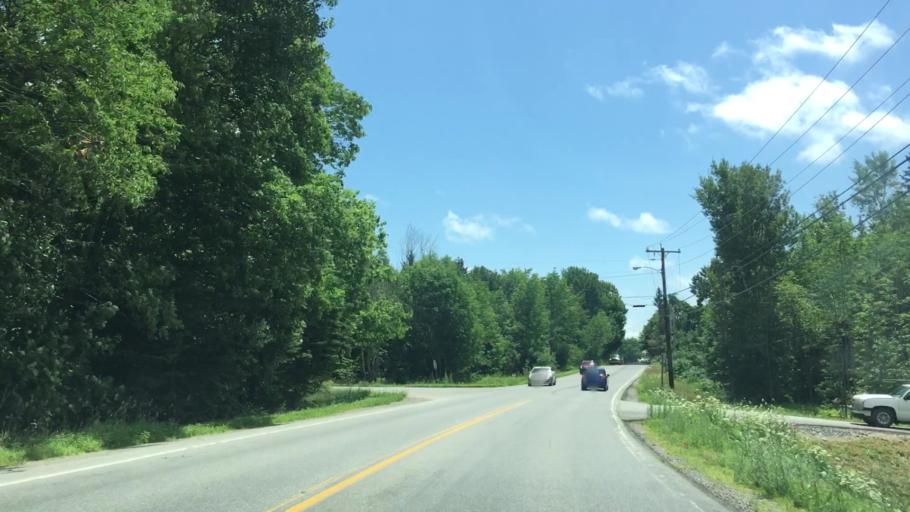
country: US
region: Maine
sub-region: Penobscot County
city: Hermon
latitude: 44.8025
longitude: -68.8956
